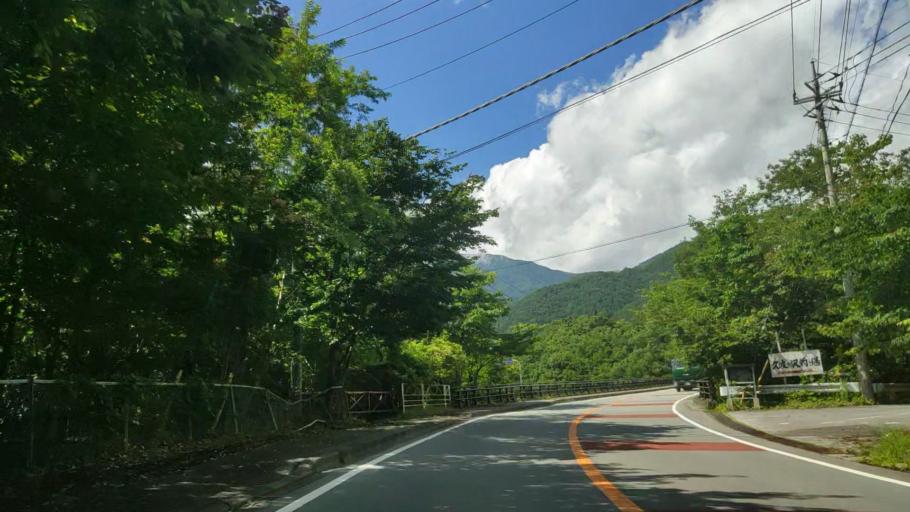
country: JP
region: Yamanashi
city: Enzan
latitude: 35.8569
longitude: 138.7568
